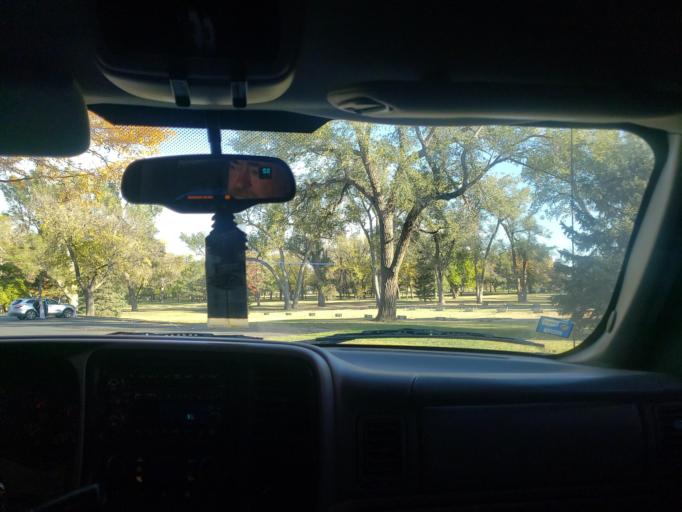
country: US
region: Kansas
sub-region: Finney County
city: Garden City
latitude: 37.9597
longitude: -100.8700
